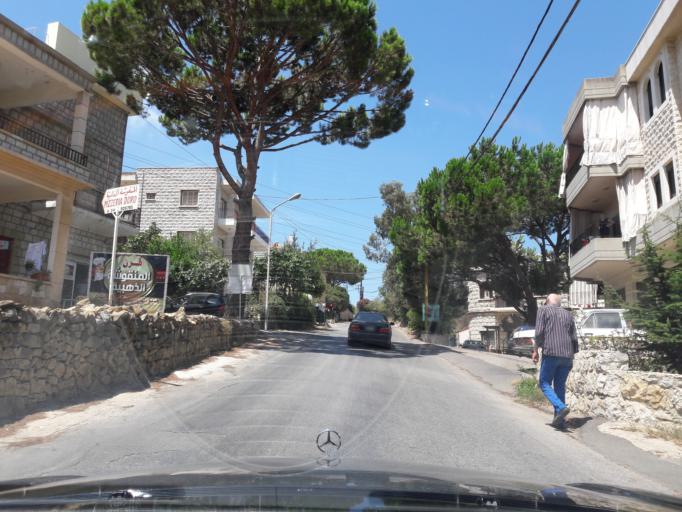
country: LB
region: Mont-Liban
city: Djounie
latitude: 33.9253
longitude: 35.6561
